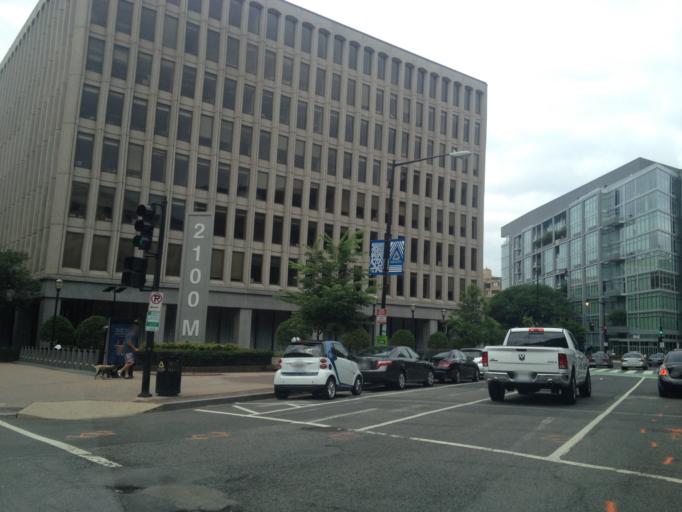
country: US
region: Washington, D.C.
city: Washington, D.C.
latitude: 38.9057
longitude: -77.0466
